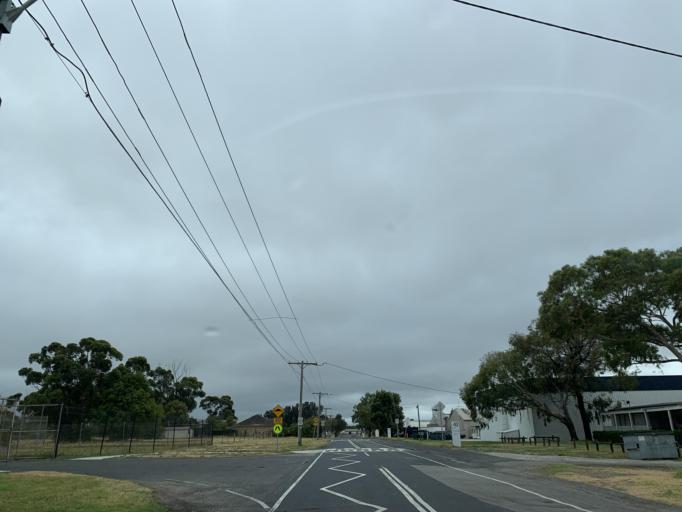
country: AU
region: Victoria
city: Heatherton
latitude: -37.9805
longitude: 145.0934
